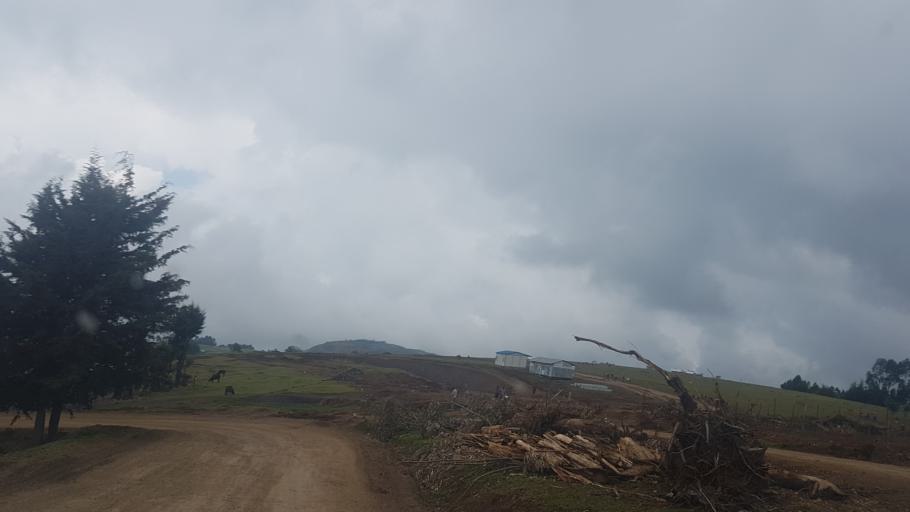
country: ET
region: Southern Nations, Nationalities, and People's Region
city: Arba Minch'
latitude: 6.3269
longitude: 37.5469
